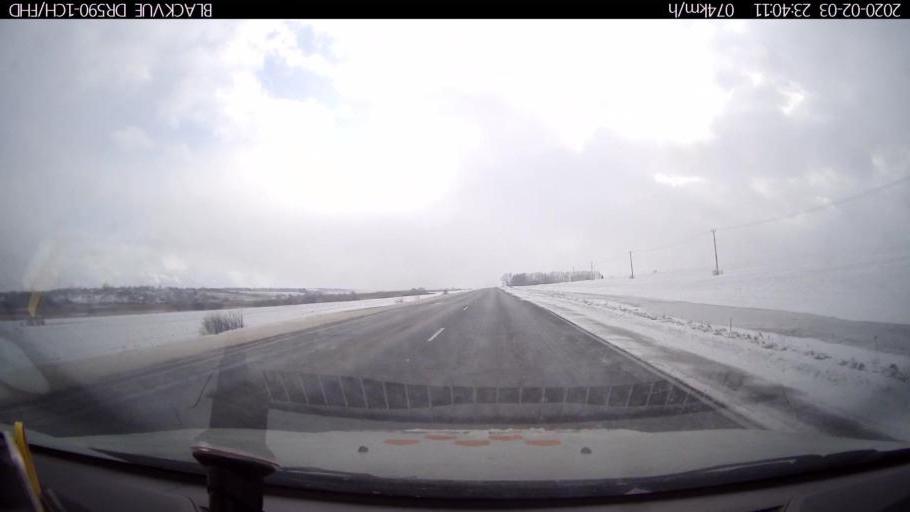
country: RU
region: Nizjnij Novgorod
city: Dal'neye Konstantinovo
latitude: 55.8759
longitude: 44.1358
